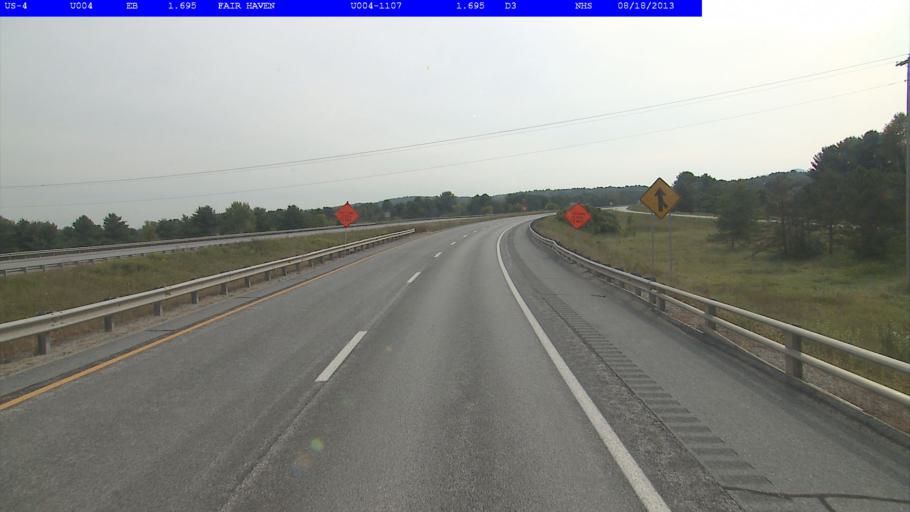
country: US
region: Vermont
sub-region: Rutland County
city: Fair Haven
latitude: 43.6056
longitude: -73.2774
